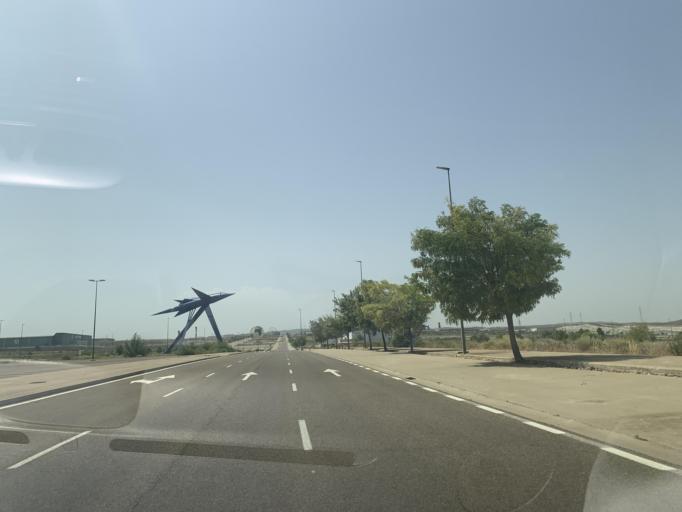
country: ES
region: Aragon
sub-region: Provincia de Zaragoza
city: Zaragoza
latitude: 41.5844
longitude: -0.8404
